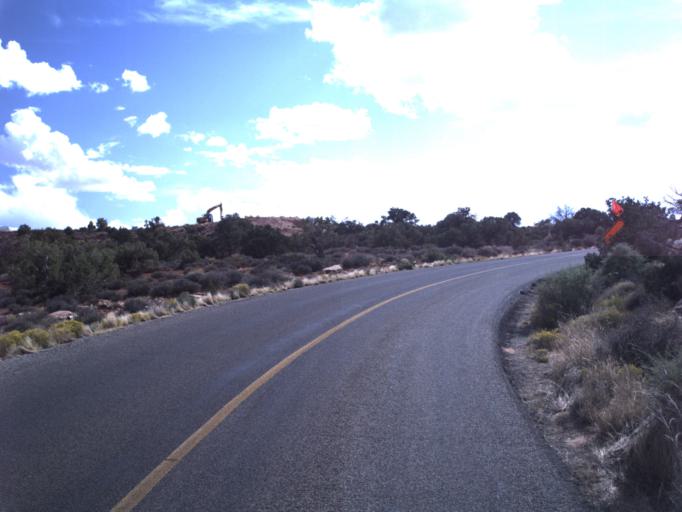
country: US
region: Utah
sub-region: Grand County
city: Moab
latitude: 38.4869
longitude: -109.7371
